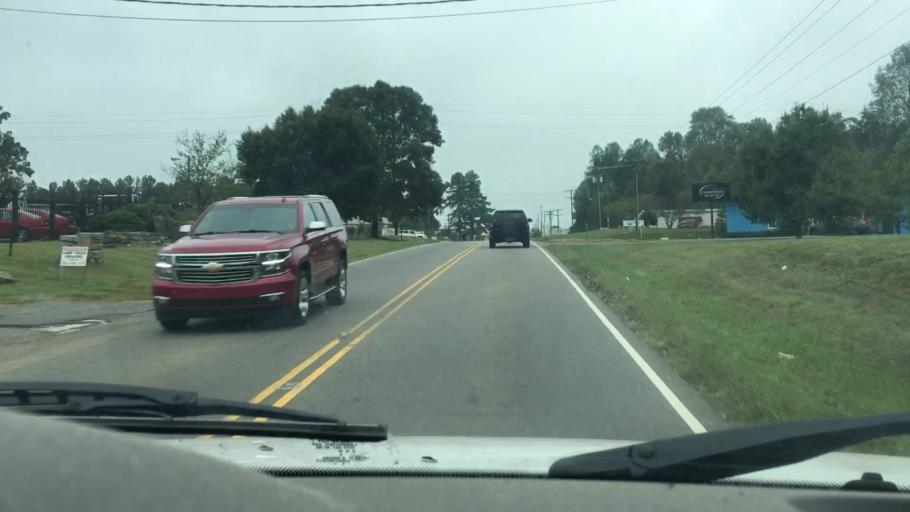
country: US
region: North Carolina
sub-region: Iredell County
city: Mooresville
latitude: 35.6042
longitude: -80.8087
